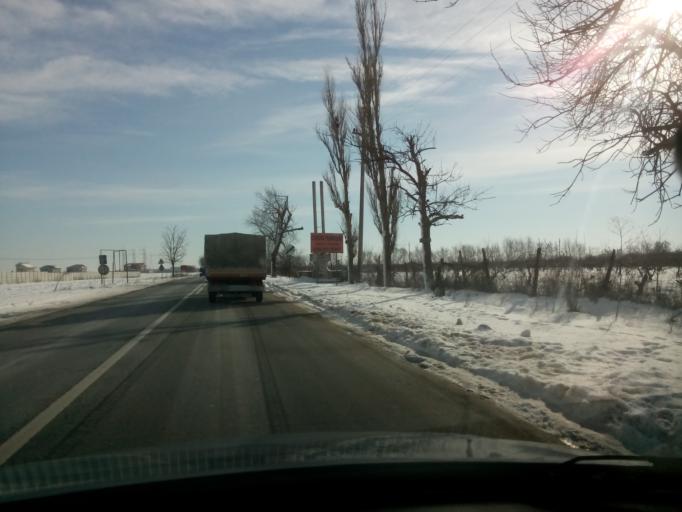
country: RO
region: Ilfov
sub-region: Comuna Glina
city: Glina
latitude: 44.3265
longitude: 26.2589
